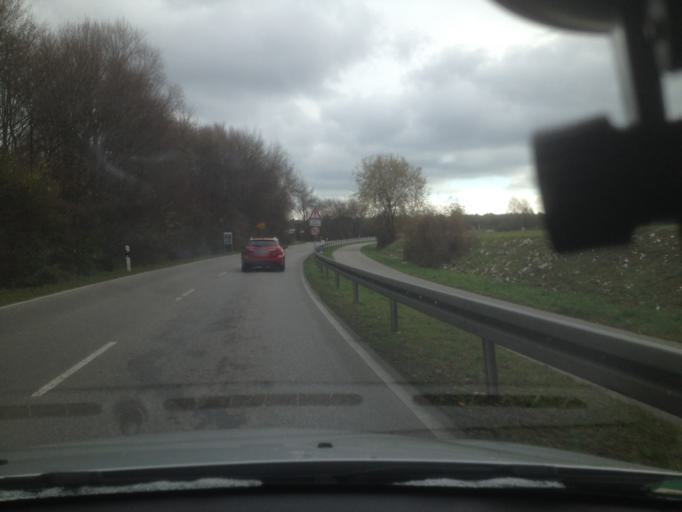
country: DE
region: Bavaria
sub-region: Swabia
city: Konigsbrunn
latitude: 48.2804
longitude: 10.8974
